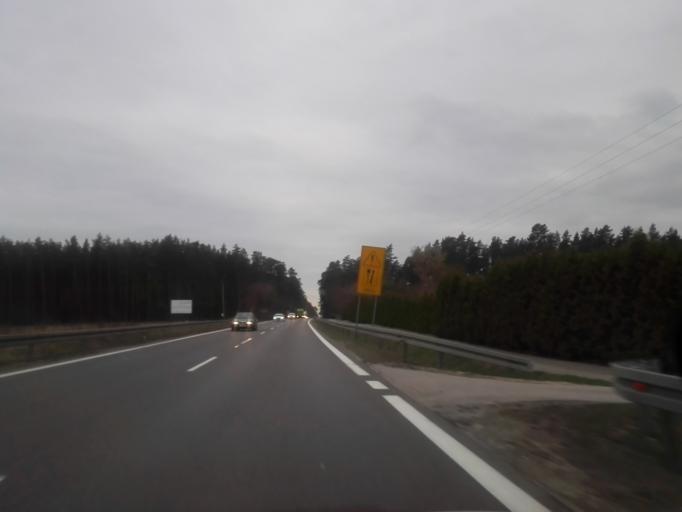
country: PL
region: Podlasie
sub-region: Powiat grajewski
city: Rajgrod
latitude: 53.7046
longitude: 22.6647
